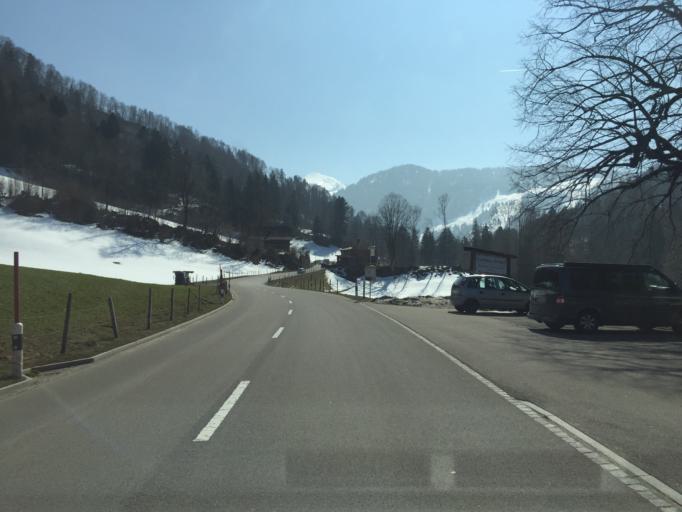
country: CH
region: Saint Gallen
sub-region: Wahlkreis Toggenburg
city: Krummenau
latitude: 47.2158
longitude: 9.2152
